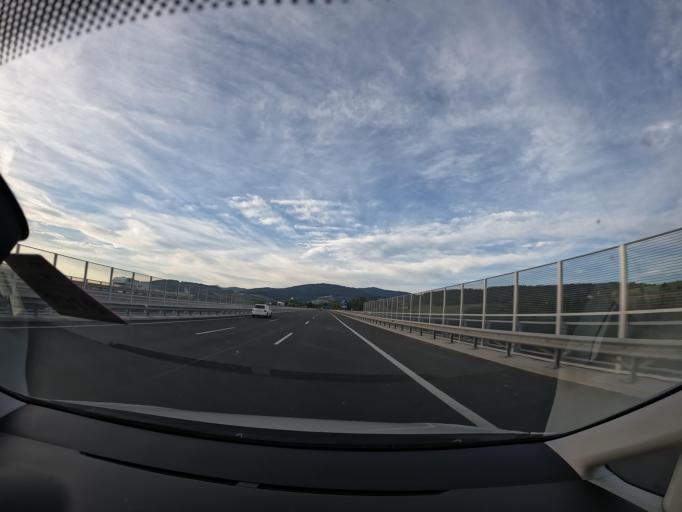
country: AT
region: Carinthia
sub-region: Politischer Bezirk Wolfsberg
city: Bad Sankt Leonhard im Lavanttal
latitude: 46.9294
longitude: 14.8223
